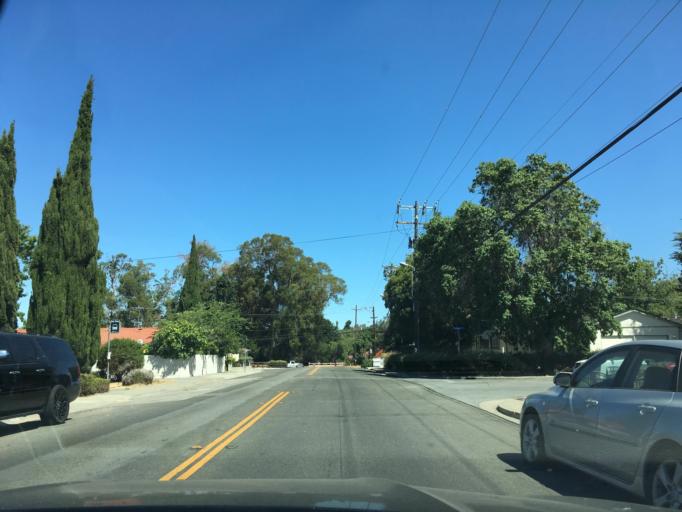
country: US
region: California
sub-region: Santa Clara County
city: East Foothills
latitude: 37.3915
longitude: -121.8334
